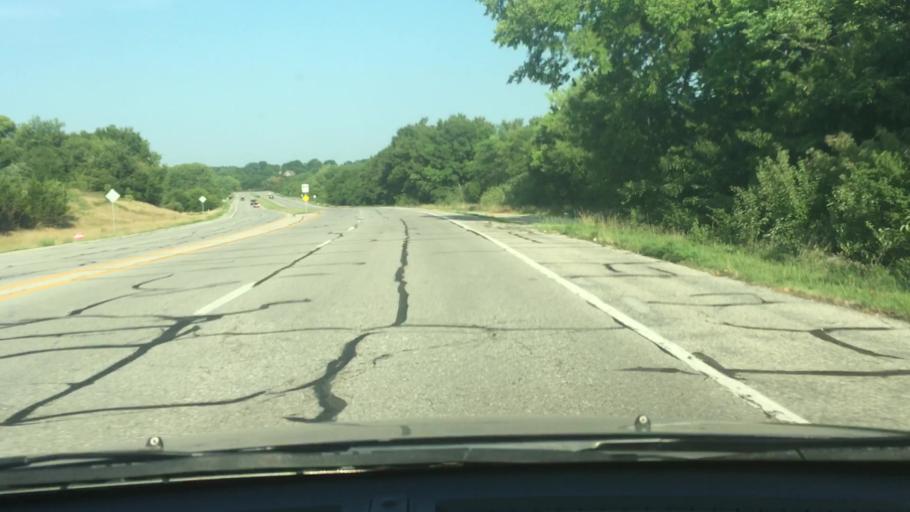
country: US
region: Missouri
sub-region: Jackson County
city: Lees Summit
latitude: 38.8914
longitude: -94.4481
